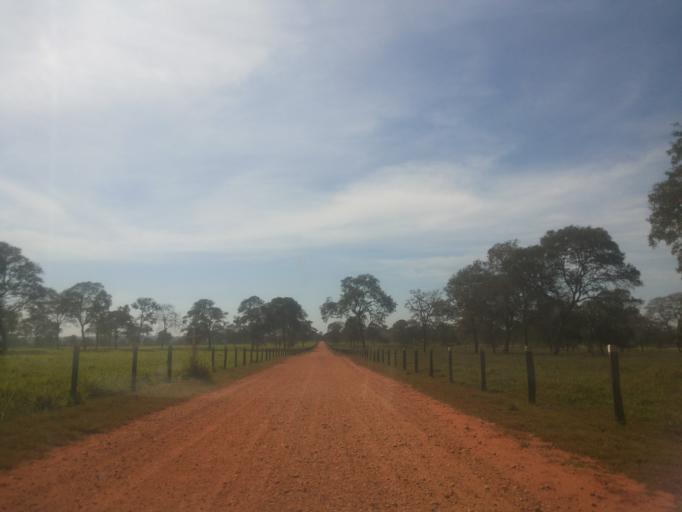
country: BR
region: Minas Gerais
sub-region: Santa Vitoria
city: Santa Vitoria
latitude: -19.0169
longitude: -50.4335
